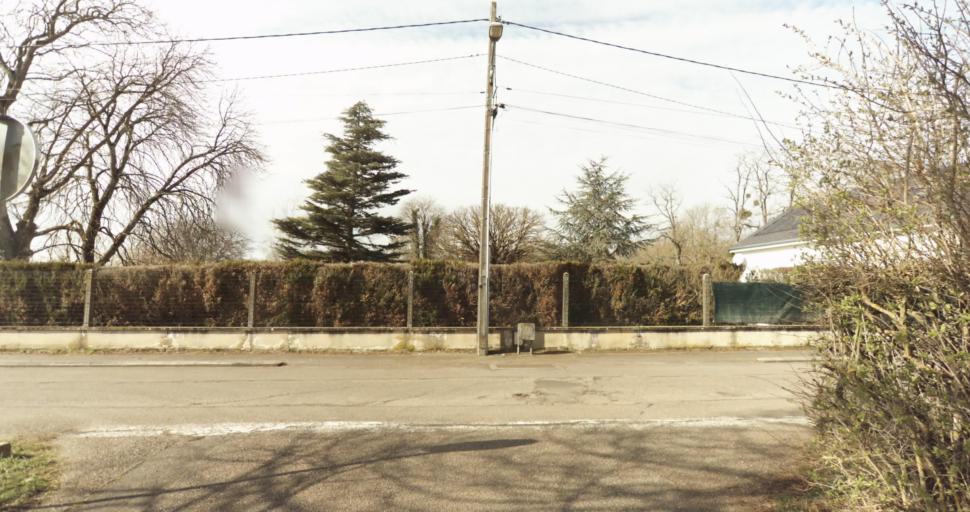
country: FR
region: Lorraine
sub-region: Departement de Meurthe-et-Moselle
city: Conflans-en-Jarnisy
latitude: 49.1514
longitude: 5.8594
